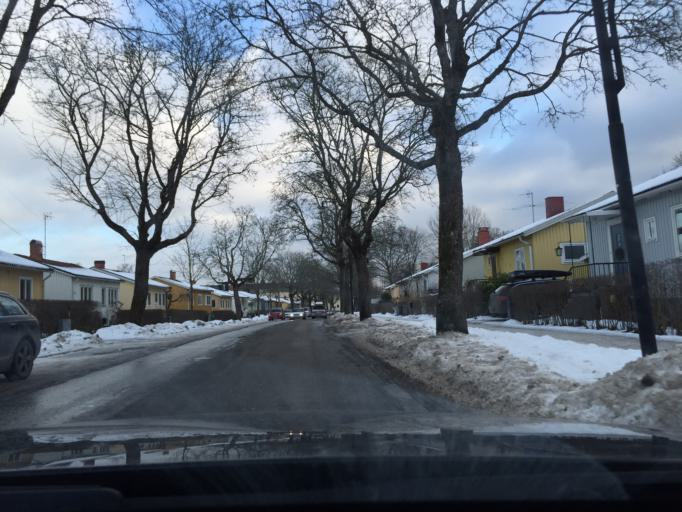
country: SE
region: Stockholm
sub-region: Stockholms Kommun
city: Bromma
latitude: 59.3446
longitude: 17.9204
